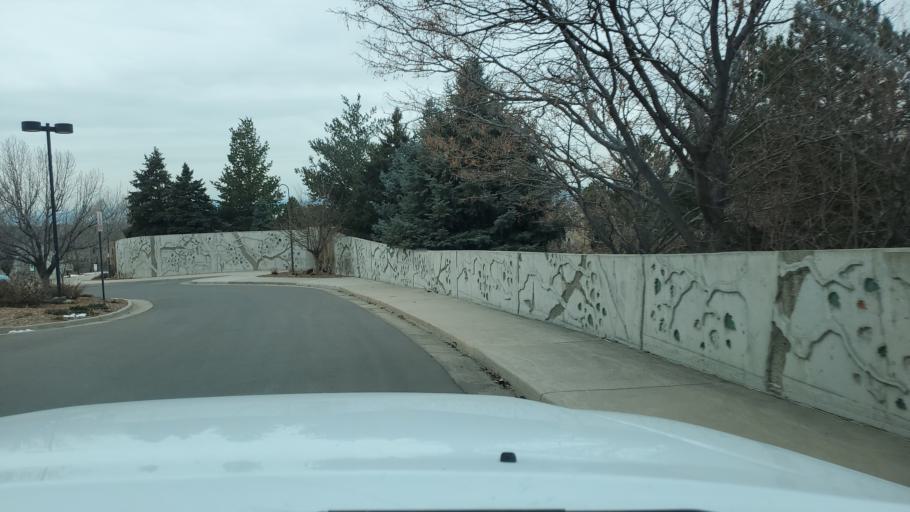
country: US
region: Colorado
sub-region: Arapahoe County
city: Castlewood
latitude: 39.6131
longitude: -104.9054
